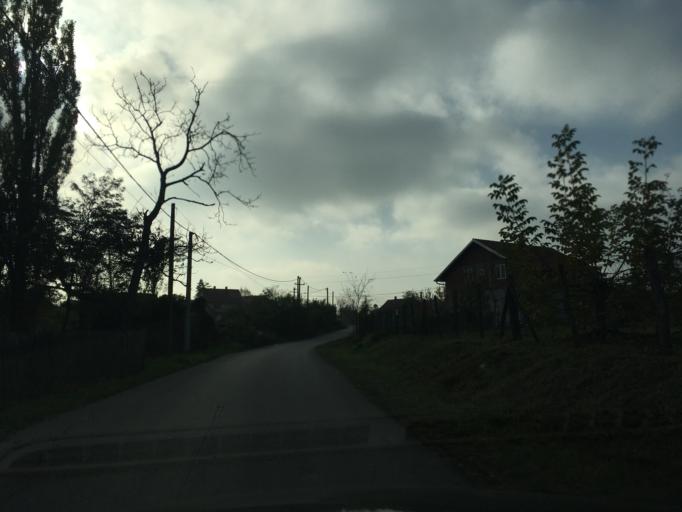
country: RS
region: Central Serbia
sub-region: Belgrade
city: Sopot
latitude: 44.4860
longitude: 20.5625
